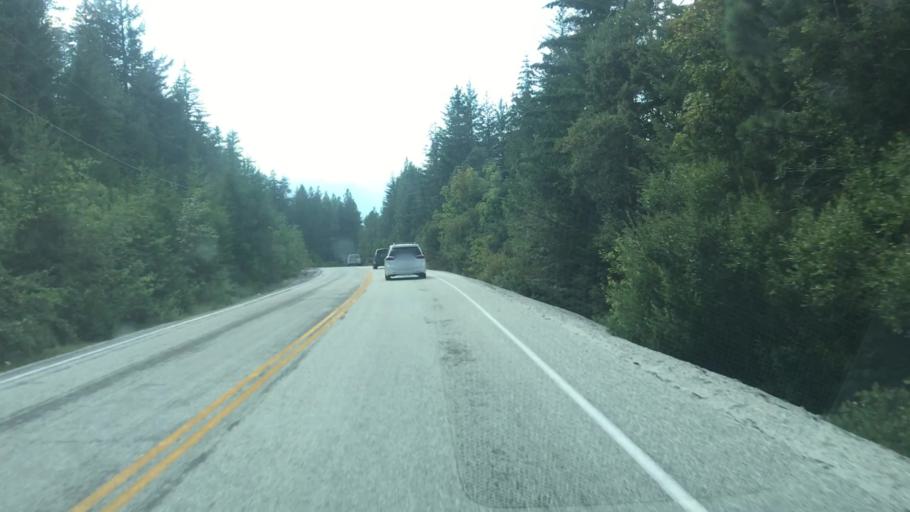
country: US
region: Washington
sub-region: Chelan County
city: Leavenworth
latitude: 47.8281
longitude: -120.7657
